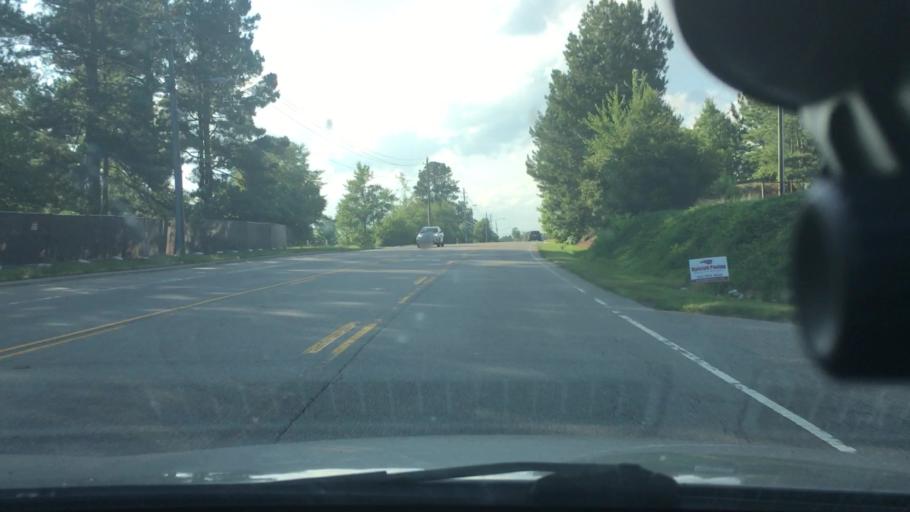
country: US
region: North Carolina
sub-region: Wake County
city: Apex
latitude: 35.7322
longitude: -78.8608
